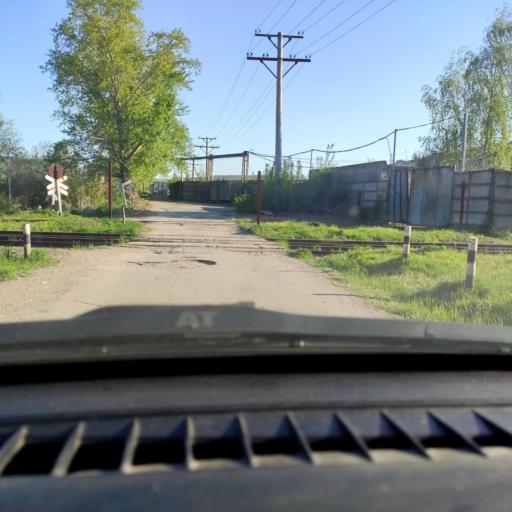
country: RU
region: Samara
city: Zhigulevsk
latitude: 53.4626
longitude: 49.5653
